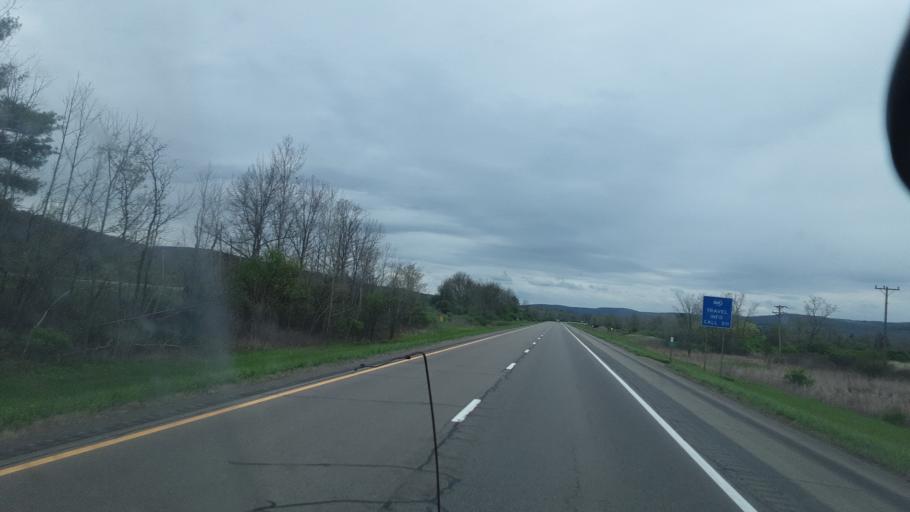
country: US
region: New York
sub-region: Allegany County
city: Belmont
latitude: 42.2375
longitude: -78.0848
